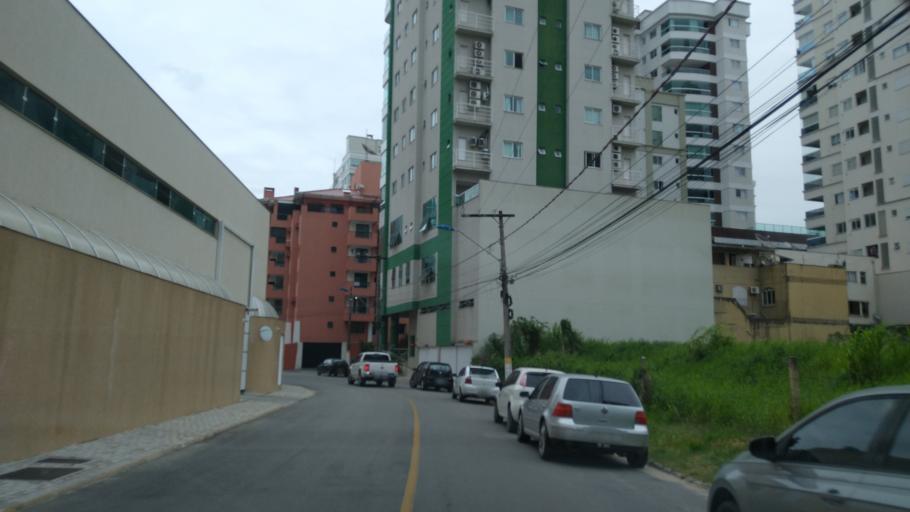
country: BR
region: Santa Catarina
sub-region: Itapema
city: Itapema
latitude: -27.0958
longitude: -48.6143
